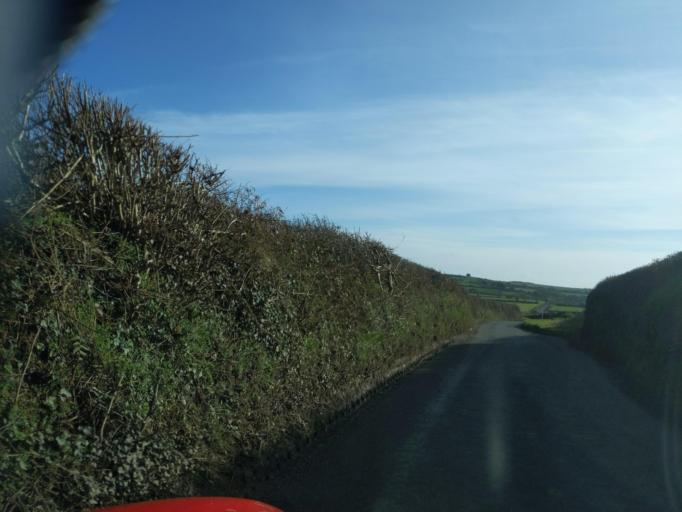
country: GB
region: England
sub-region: Devon
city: Kingsbridge
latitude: 50.3405
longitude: -3.7239
